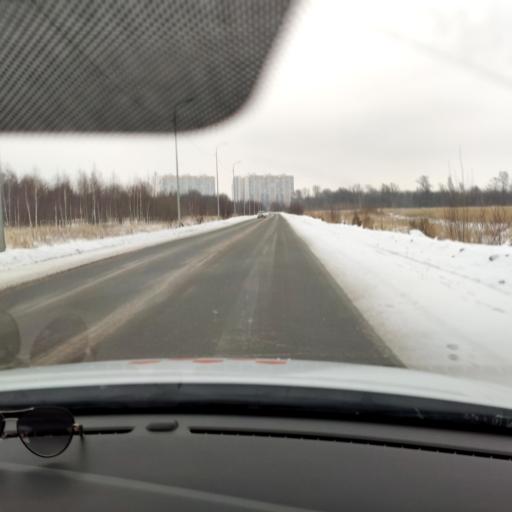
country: RU
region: Tatarstan
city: Stolbishchi
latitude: 55.7145
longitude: 49.1703
